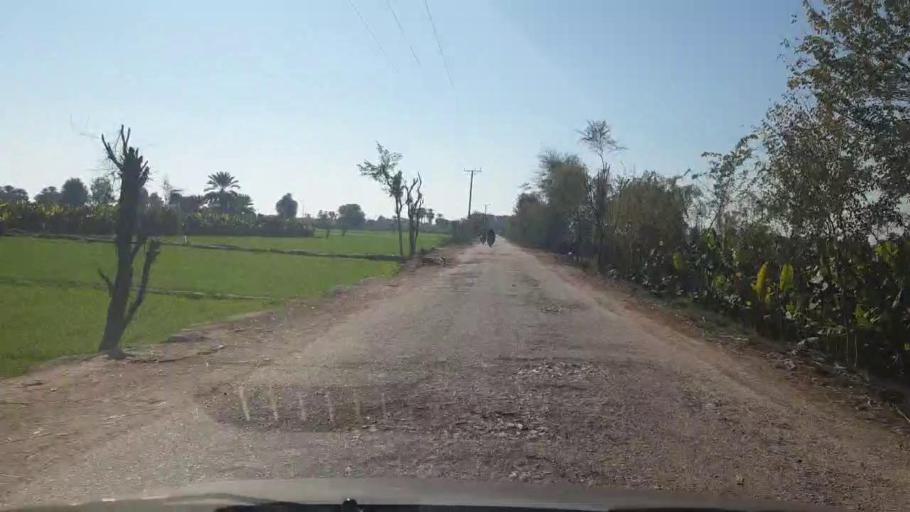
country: PK
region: Sindh
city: Bozdar
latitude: 27.2533
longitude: 68.6522
